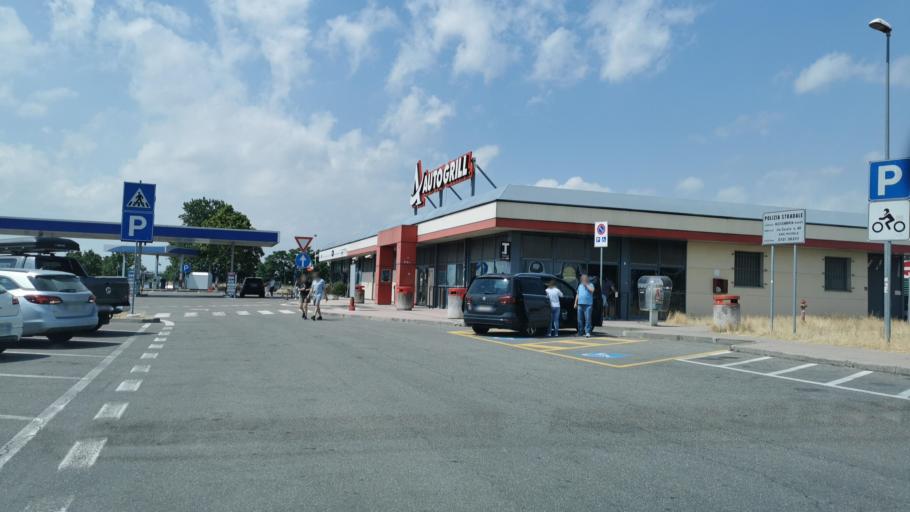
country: IT
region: Piedmont
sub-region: Provincia di Alessandria
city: Tortona
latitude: 44.9357
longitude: 8.8841
